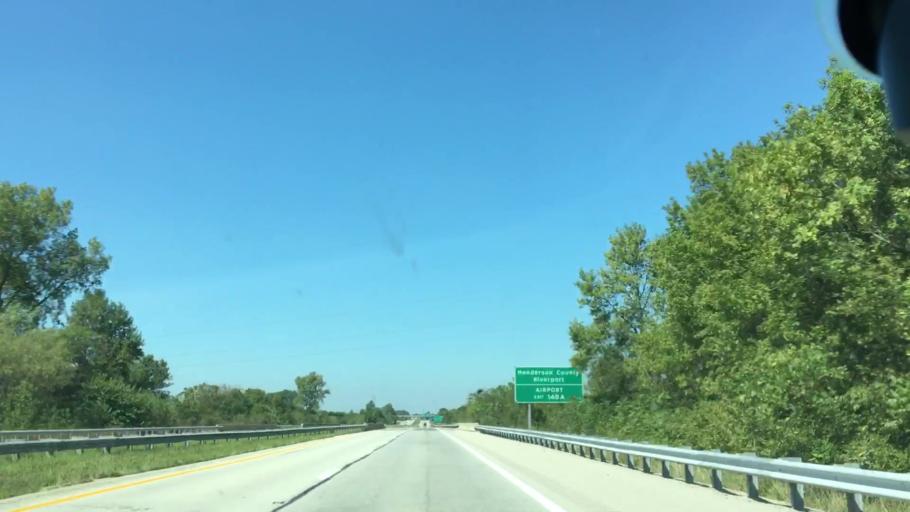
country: US
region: Kentucky
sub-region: Henderson County
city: Henderson
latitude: 37.7855
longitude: -87.5485
